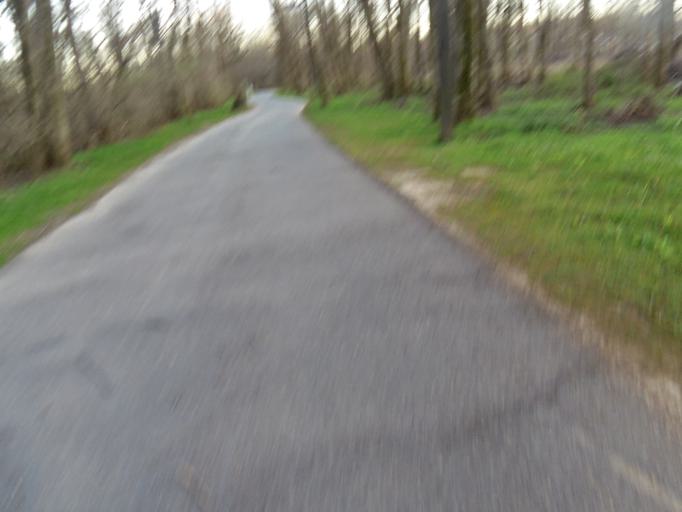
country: US
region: Tennessee
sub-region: Blount County
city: Maryville
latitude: 35.7618
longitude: -83.9820
